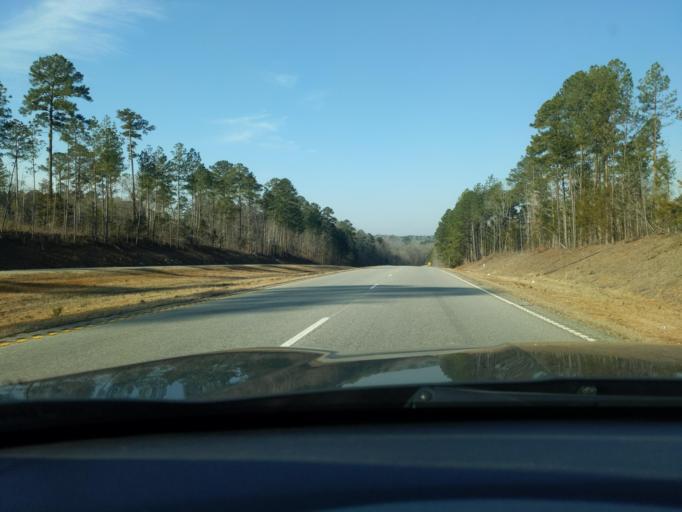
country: US
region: South Carolina
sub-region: Abbeville County
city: Abbeville
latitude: 34.1839
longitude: -82.2961
